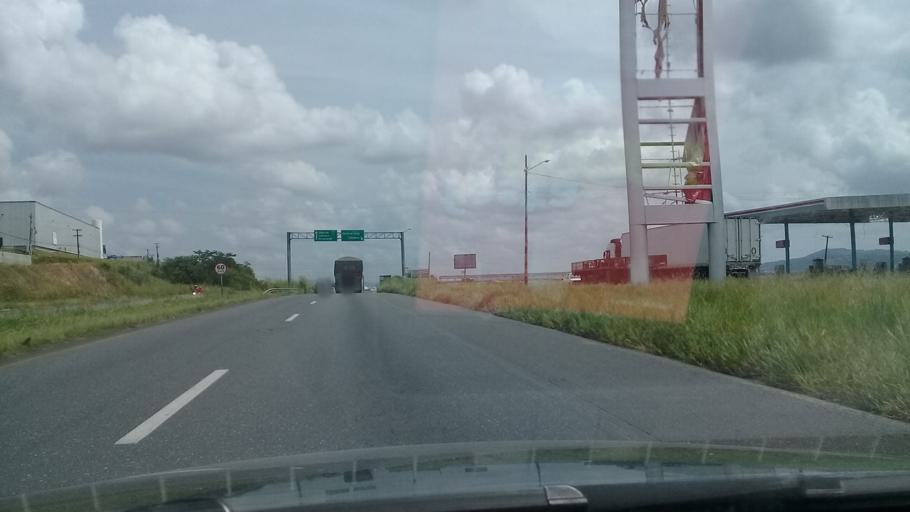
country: BR
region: Pernambuco
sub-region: Vitoria De Santo Antao
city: Vitoria de Santo Antao
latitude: -8.1162
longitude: -35.2560
